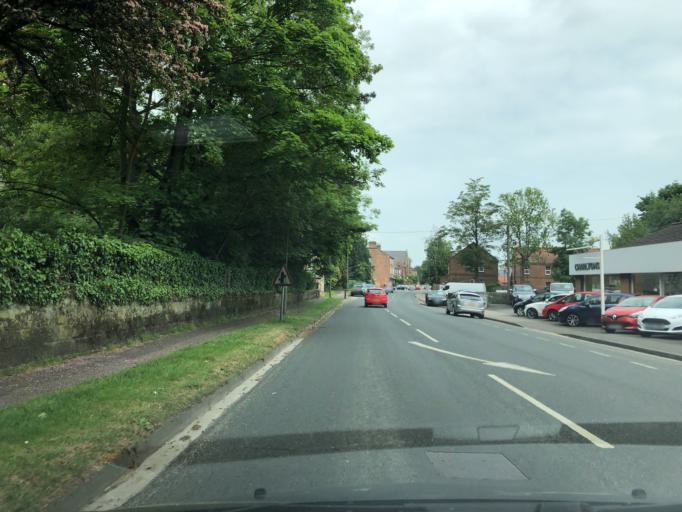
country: GB
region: England
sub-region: North Yorkshire
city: Boroughbridge
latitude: 54.0921
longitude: -1.3982
